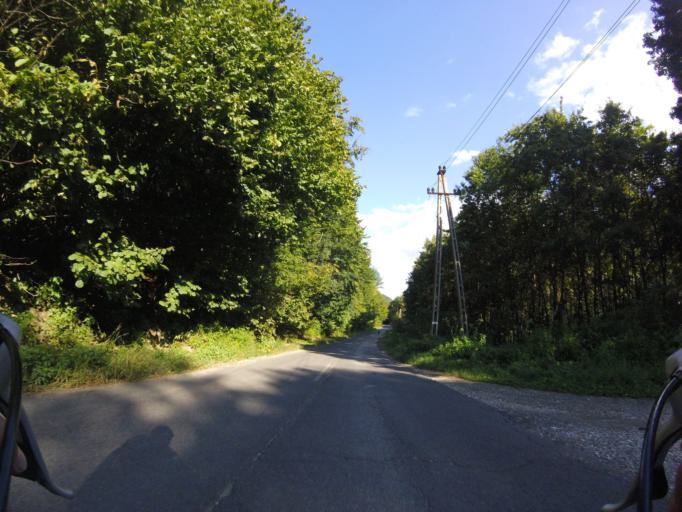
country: HU
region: Borsod-Abauj-Zemplen
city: Kazincbarcika
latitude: 48.1174
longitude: 20.5722
